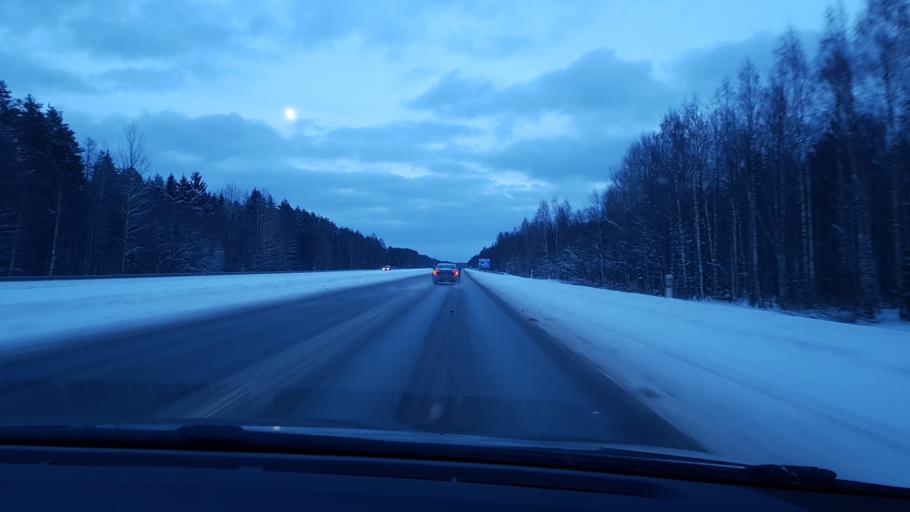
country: EE
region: Harju
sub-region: Kuusalu vald
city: Kuusalu
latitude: 59.4593
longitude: 25.5731
